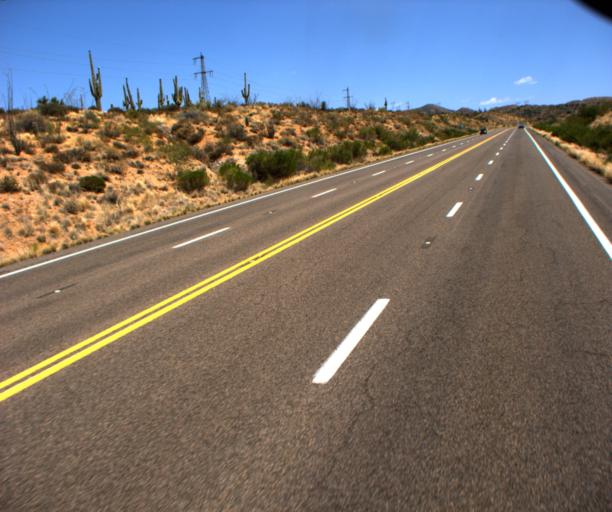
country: US
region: Arizona
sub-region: Gila County
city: Miami
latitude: 33.5751
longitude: -110.9575
